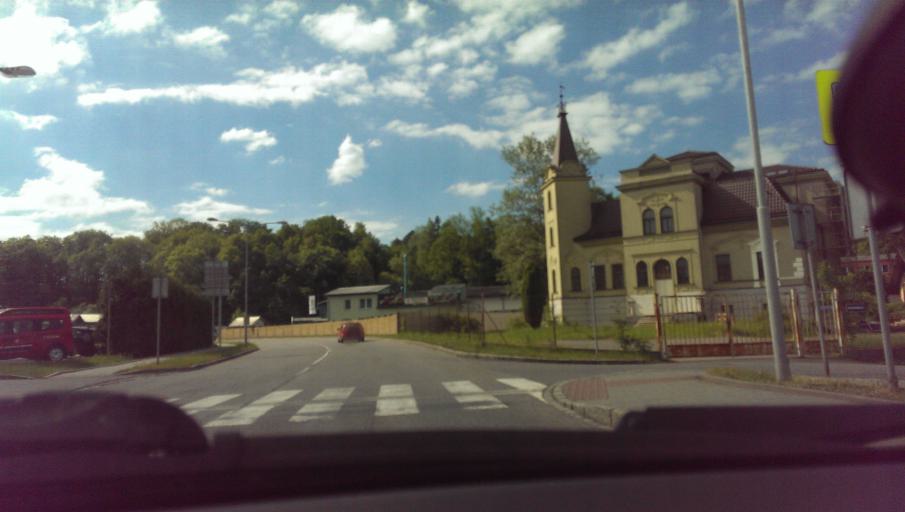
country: CZ
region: Zlin
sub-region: Okres Vsetin
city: Roznov pod Radhostem
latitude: 49.4580
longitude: 18.1392
